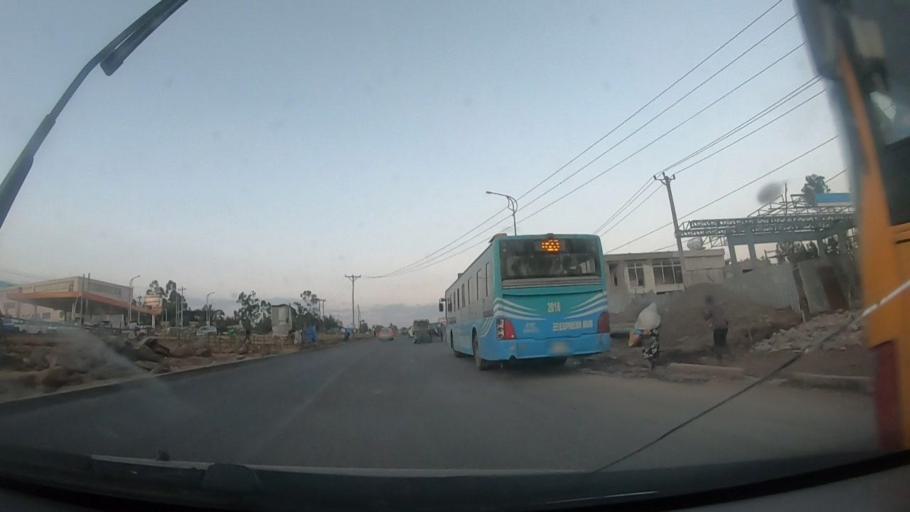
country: ET
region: Adis Abeba
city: Addis Ababa
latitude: 9.0551
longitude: 38.8781
